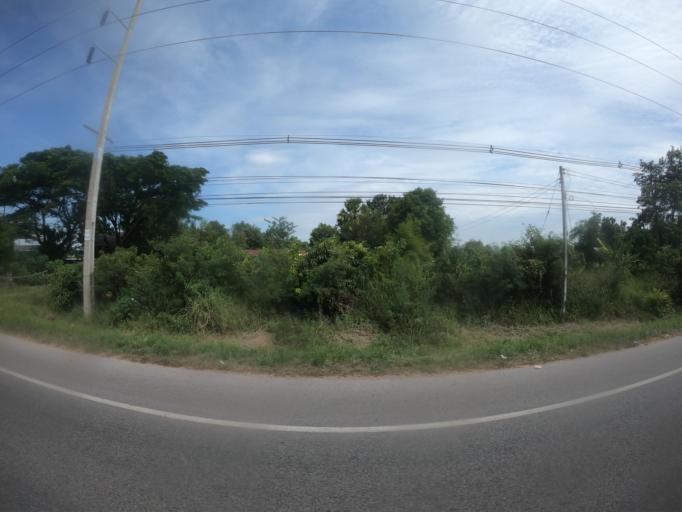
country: TH
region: Maha Sarakham
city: Chiang Yuen
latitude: 16.4252
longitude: 103.0686
